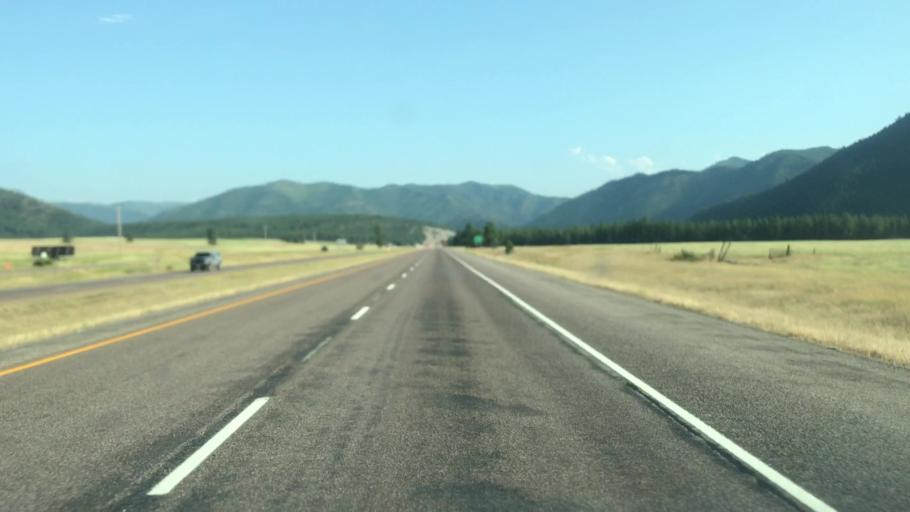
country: US
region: Montana
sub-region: Mineral County
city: Superior
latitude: 47.0446
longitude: -114.7520
